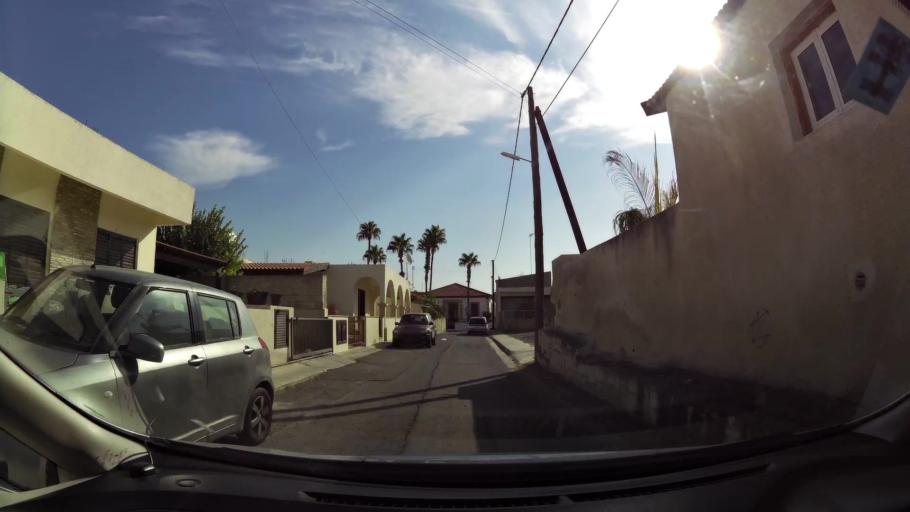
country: CY
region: Larnaka
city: Aradippou
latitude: 34.9506
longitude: 33.5913
